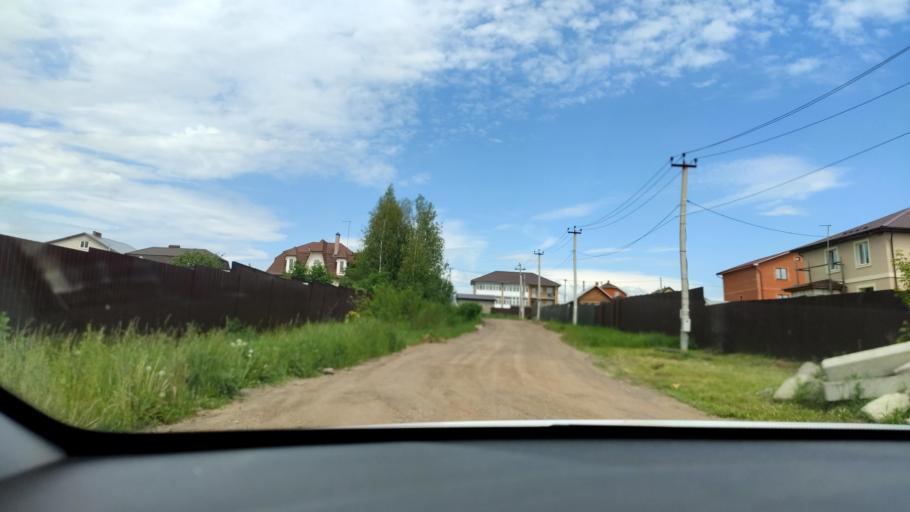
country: RU
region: Tatarstan
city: Stolbishchi
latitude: 55.7133
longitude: 49.3706
